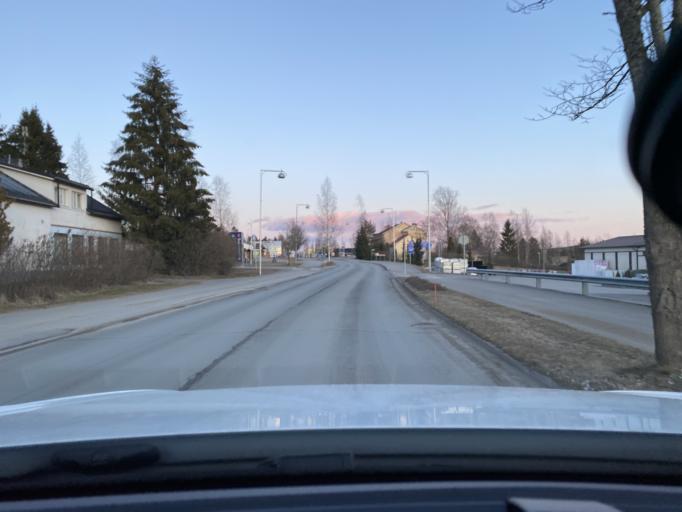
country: FI
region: Pirkanmaa
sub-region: Lounais-Pirkanmaa
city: Punkalaidun
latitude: 61.1127
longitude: 23.1025
